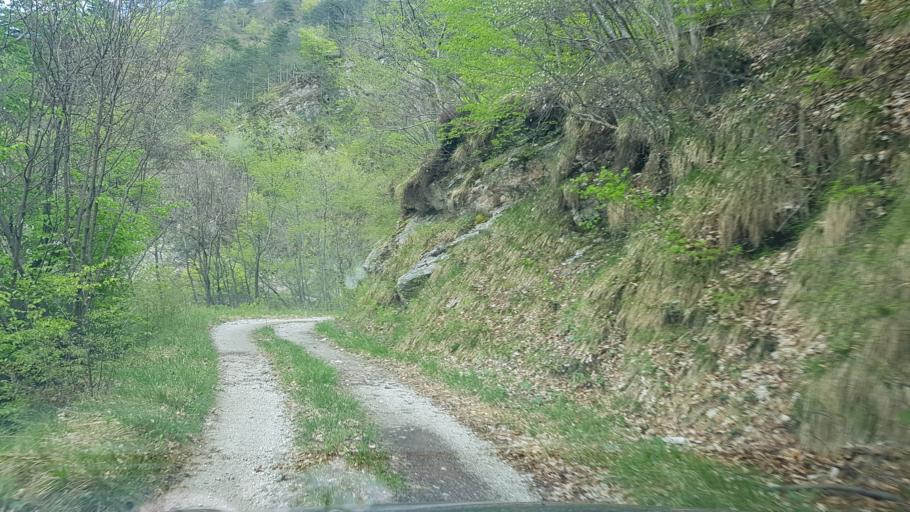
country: IT
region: Friuli Venezia Giulia
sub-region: Provincia di Udine
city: Cavazzo Carnico
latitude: 46.3104
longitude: 13.0096
